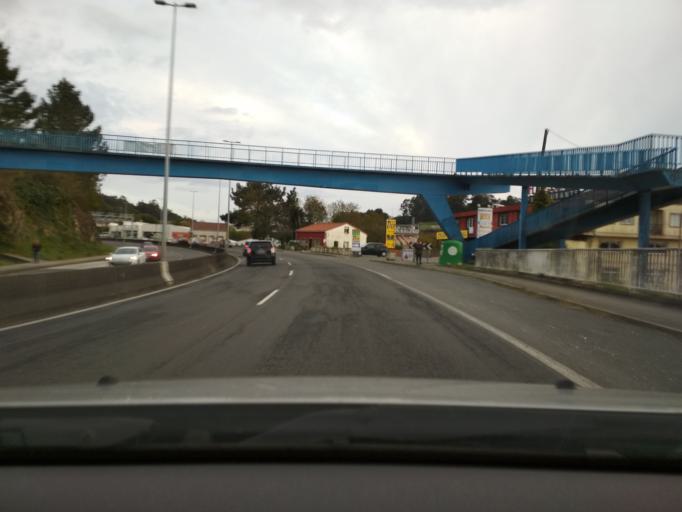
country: ES
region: Galicia
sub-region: Provincia da Coruna
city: Santiago de Compostela
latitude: 42.8596
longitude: -8.5718
